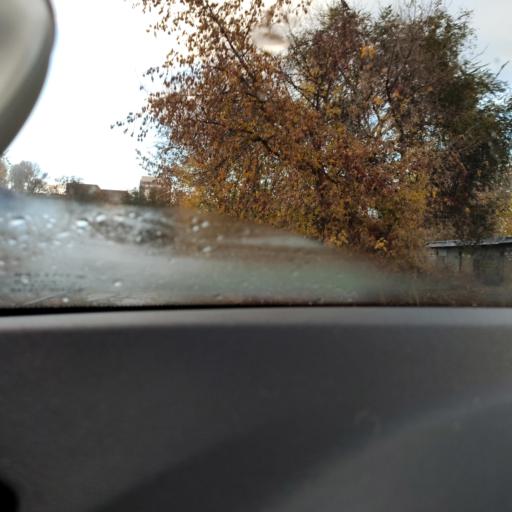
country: RU
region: Samara
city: Smyshlyayevka
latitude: 53.2048
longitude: 50.2853
